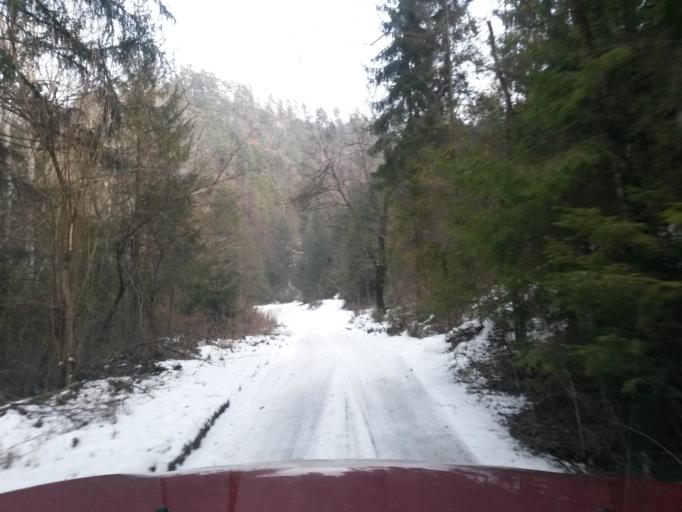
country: SK
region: Kosicky
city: Spisska Nova Ves
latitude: 48.8949
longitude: 20.6389
